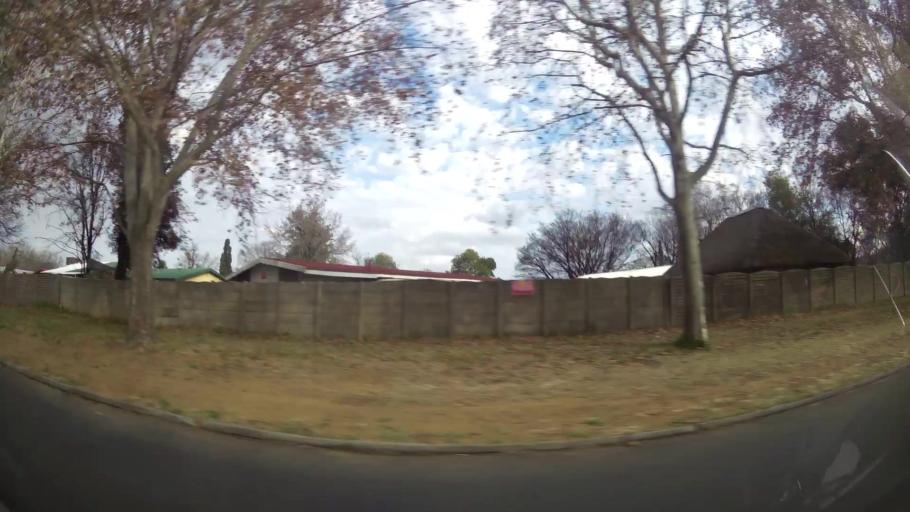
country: ZA
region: Orange Free State
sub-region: Fezile Dabi District Municipality
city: Sasolburg
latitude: -26.8102
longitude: 27.8228
